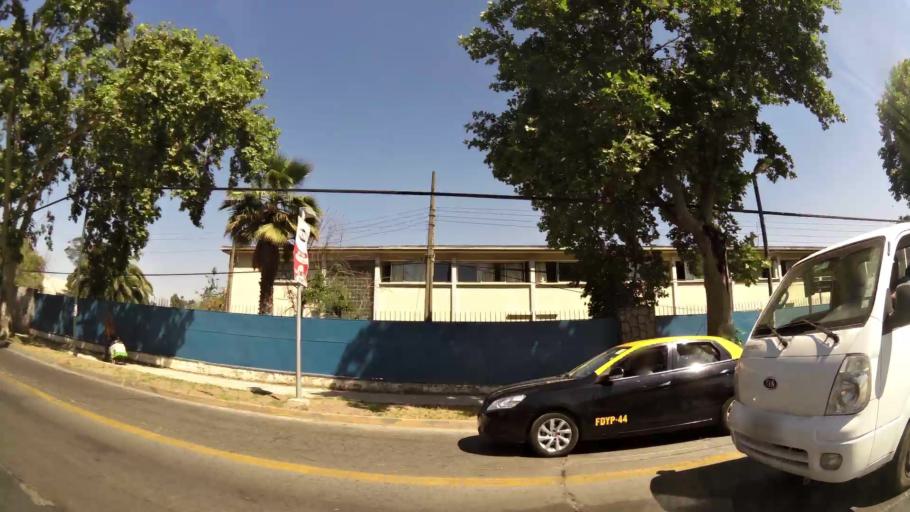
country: CL
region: Santiago Metropolitan
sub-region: Provincia de Maipo
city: San Bernardo
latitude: -33.5584
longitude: -70.6784
